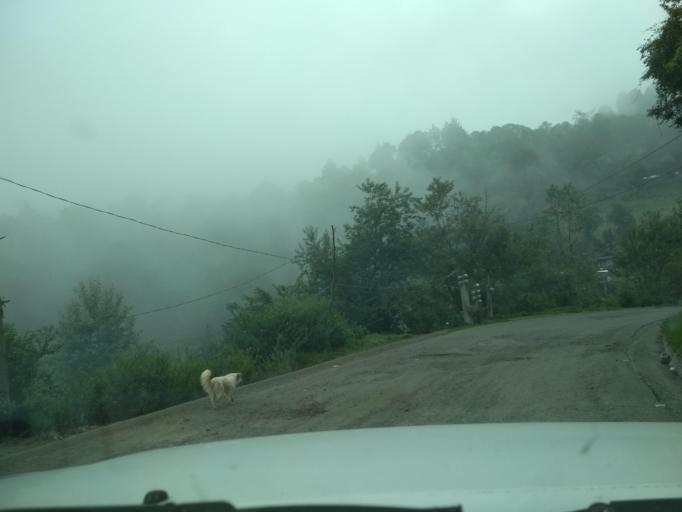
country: MX
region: Veracruz
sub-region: La Perla
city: Chilapa
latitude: 18.9713
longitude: -97.1719
